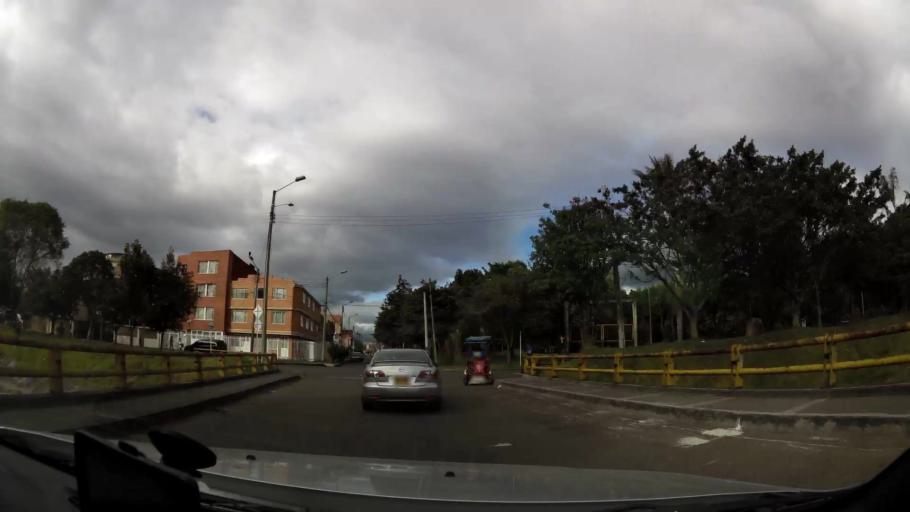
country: CO
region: Bogota D.C.
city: Bogota
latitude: 4.6031
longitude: -74.1175
